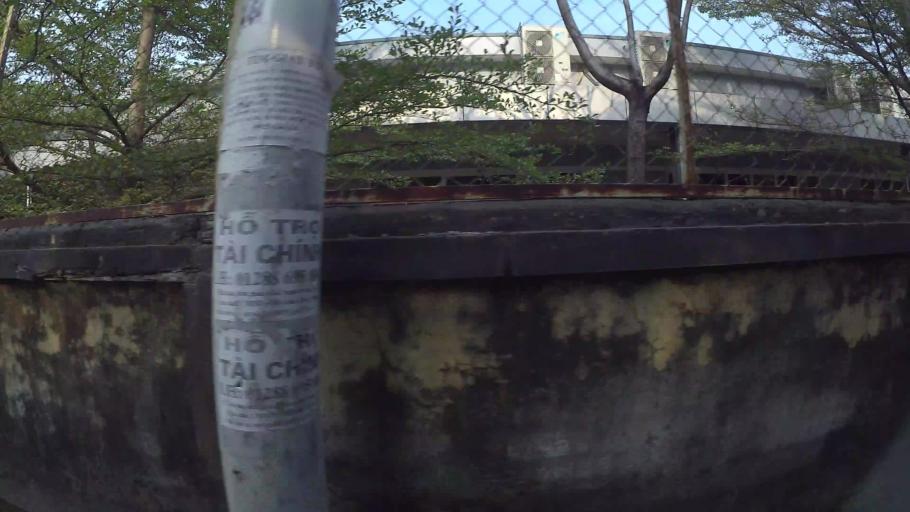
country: VN
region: Da Nang
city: Lien Chieu
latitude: 16.0496
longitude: 108.1580
